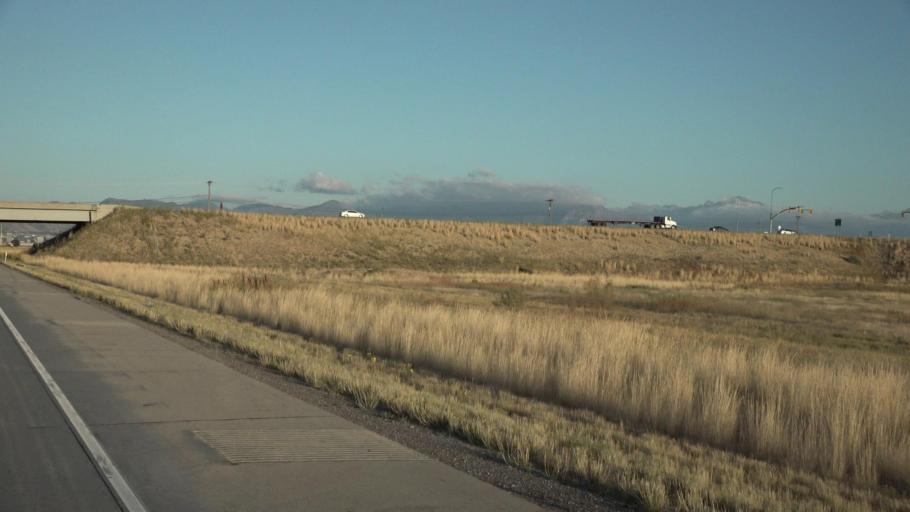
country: US
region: Utah
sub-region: Salt Lake County
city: West Valley City
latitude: 40.7709
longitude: -112.0270
